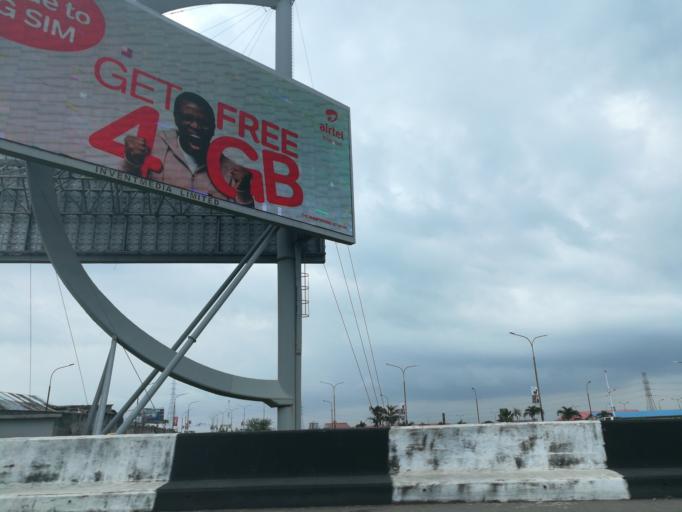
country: NG
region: Lagos
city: Lagos
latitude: 6.4616
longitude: 3.3951
